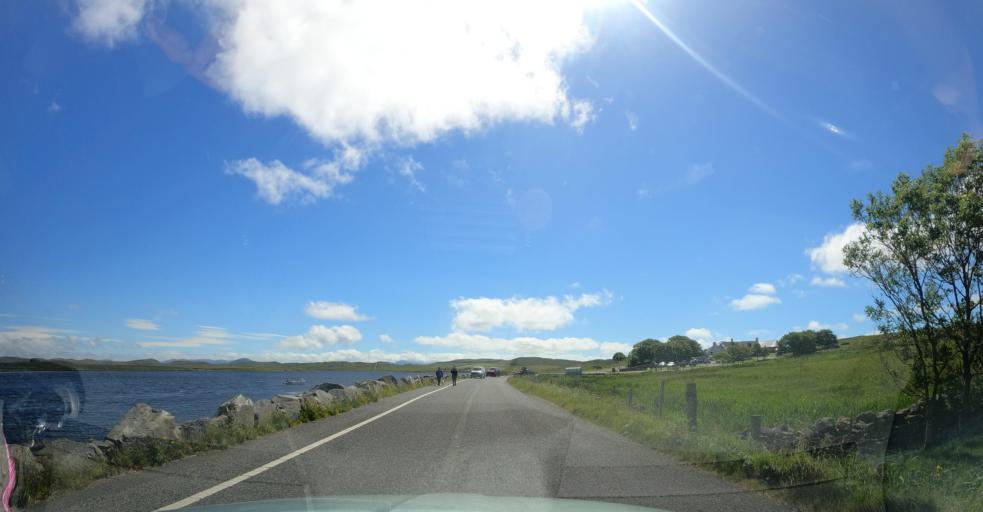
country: GB
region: Scotland
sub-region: Eilean Siar
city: Harris
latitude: 58.1965
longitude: -6.7415
